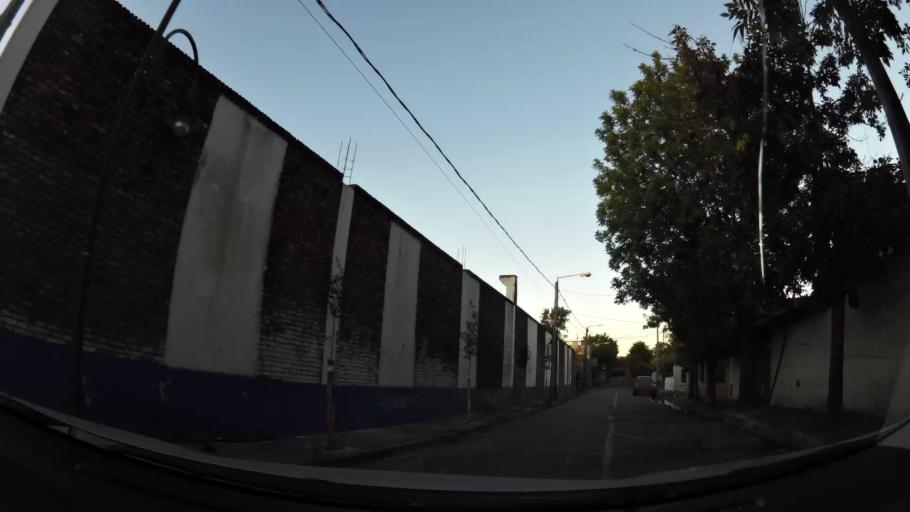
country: AR
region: Buenos Aires
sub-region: Partido de Tigre
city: Tigre
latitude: -34.4395
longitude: -58.5709
